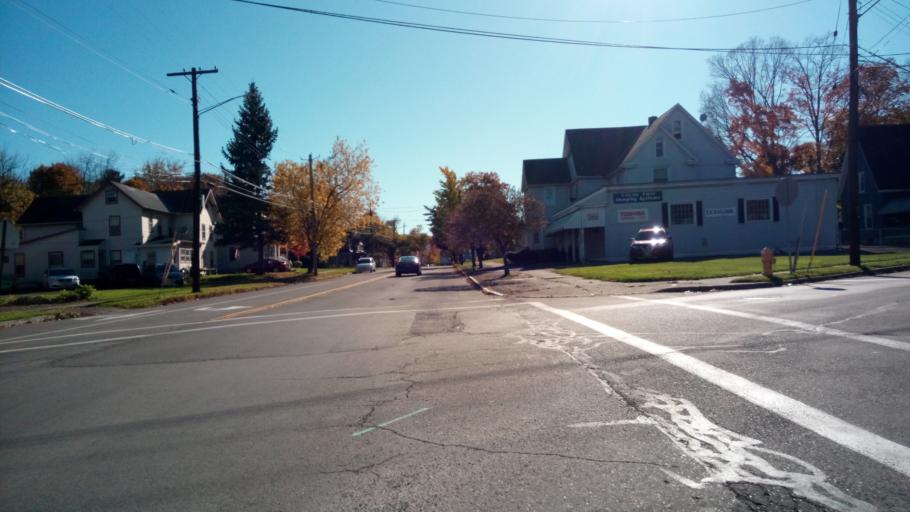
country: US
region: New York
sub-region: Chemung County
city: Elmira
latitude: 42.0775
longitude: -76.8034
